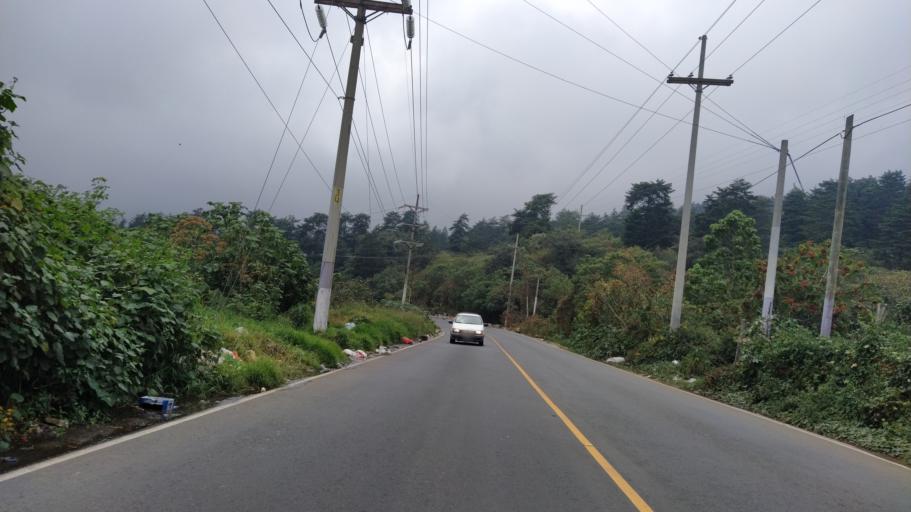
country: GT
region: Quetzaltenango
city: Zunil
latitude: 14.7451
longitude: -91.5142
